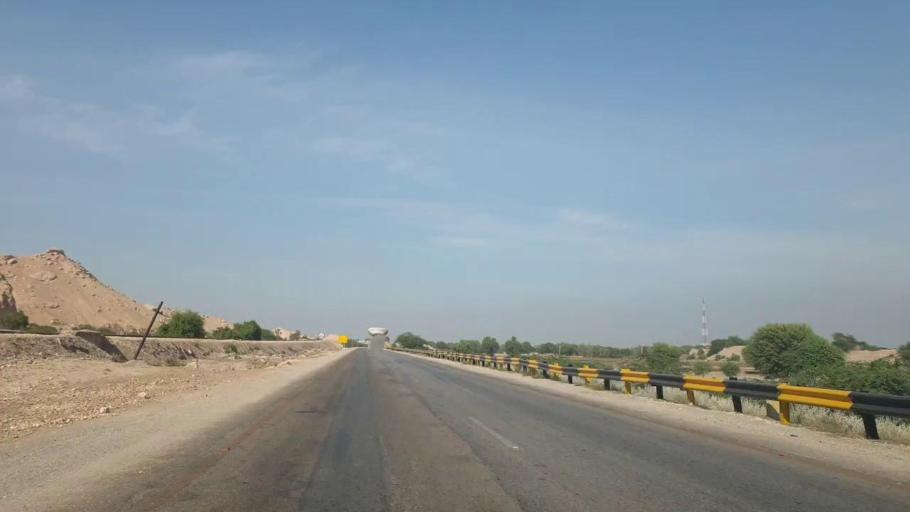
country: PK
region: Sindh
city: Sehwan
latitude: 26.2942
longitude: 67.8944
